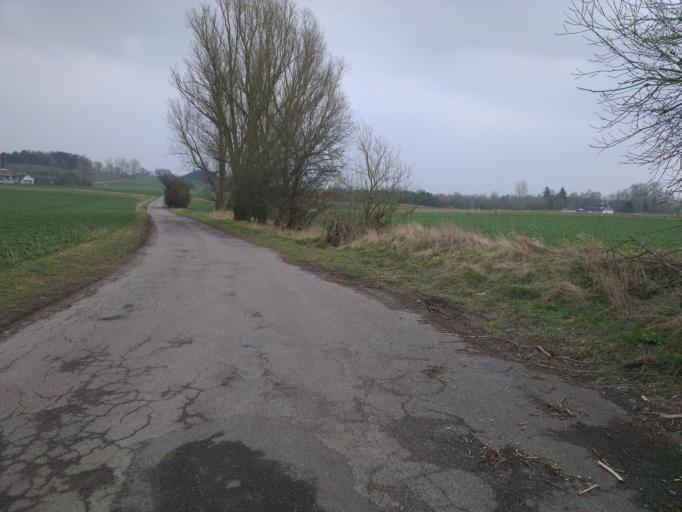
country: DK
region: Capital Region
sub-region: Frederikssund Kommune
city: Jaegerspris
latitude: 55.8250
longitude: 12.0143
